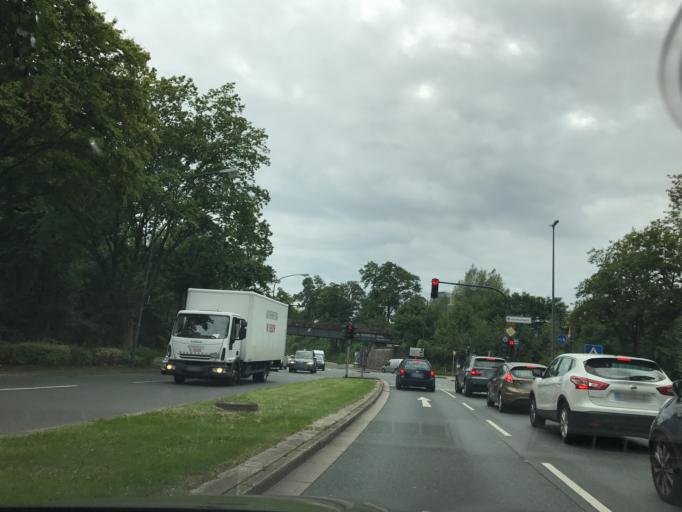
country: DE
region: North Rhine-Westphalia
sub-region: Regierungsbezirk Dusseldorf
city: Essen
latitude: 51.4646
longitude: 6.9993
